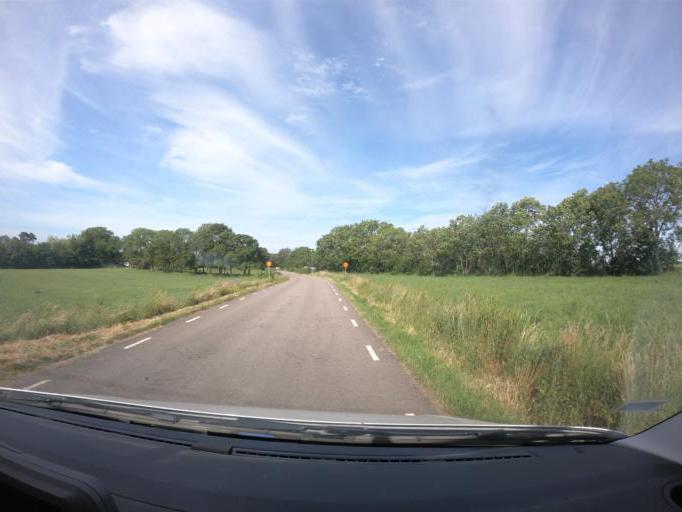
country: SE
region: Skane
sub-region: Angelholms Kommun
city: Vejbystrand
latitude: 56.3965
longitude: 12.6755
